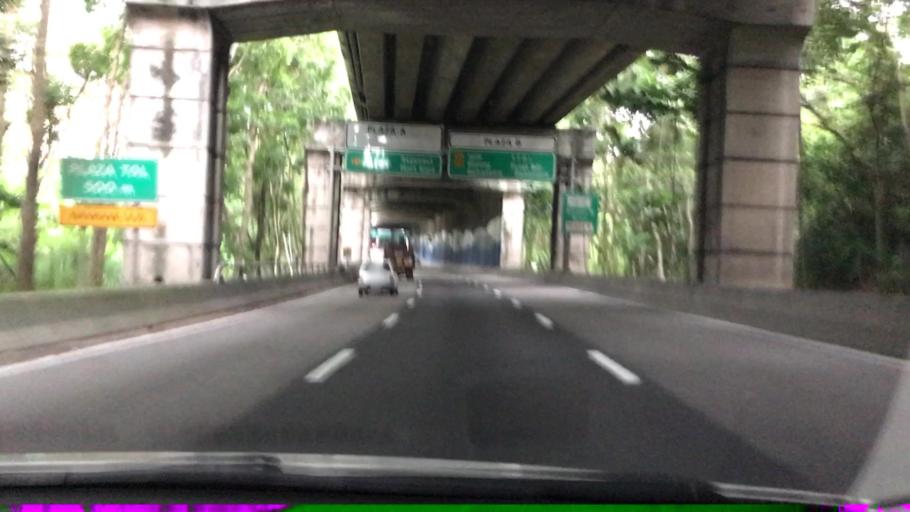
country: MY
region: Kuala Lumpur
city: Kuala Lumpur
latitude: 3.1243
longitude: 101.6618
